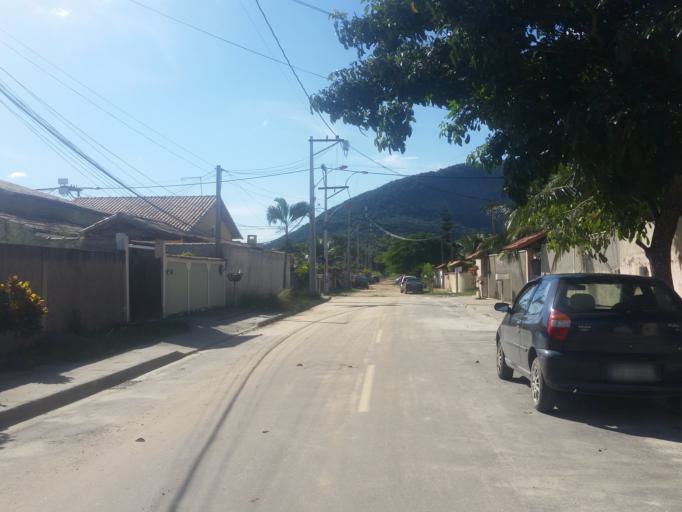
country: BR
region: Rio de Janeiro
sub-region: Marica
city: Marica
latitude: -22.9601
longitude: -42.9658
